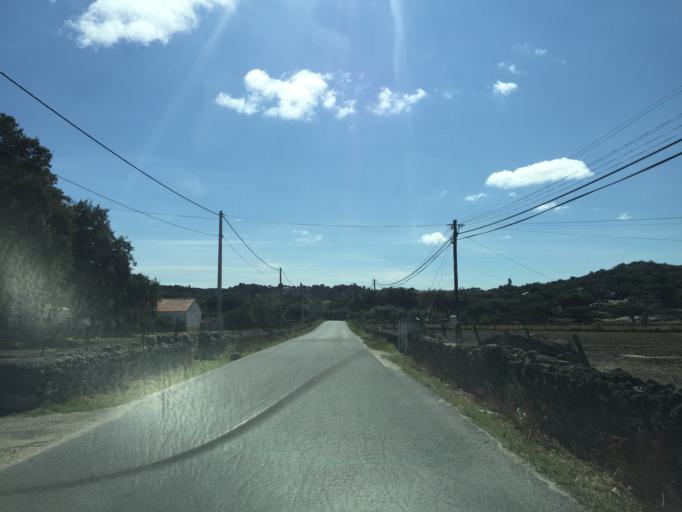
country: PT
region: Portalegre
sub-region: Marvao
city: Marvao
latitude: 39.4281
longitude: -7.3567
